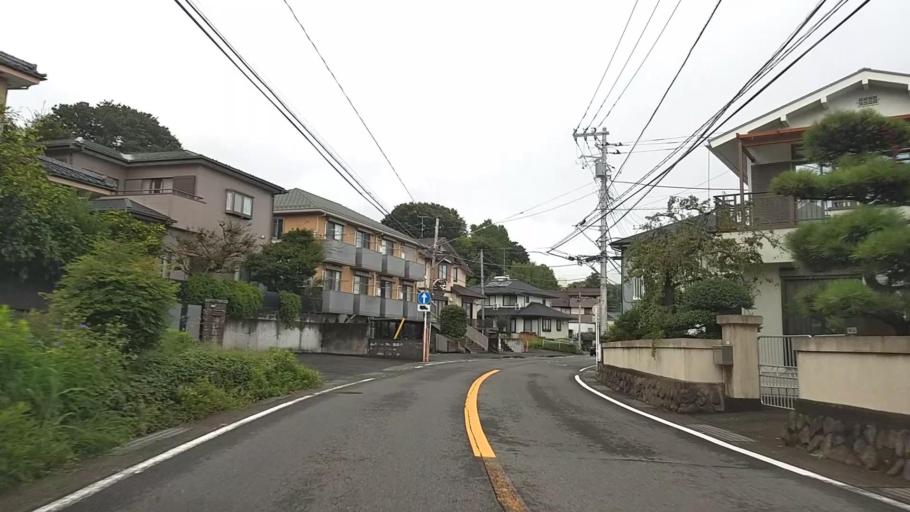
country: JP
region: Kanagawa
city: Atsugi
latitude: 35.4486
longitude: 139.3520
